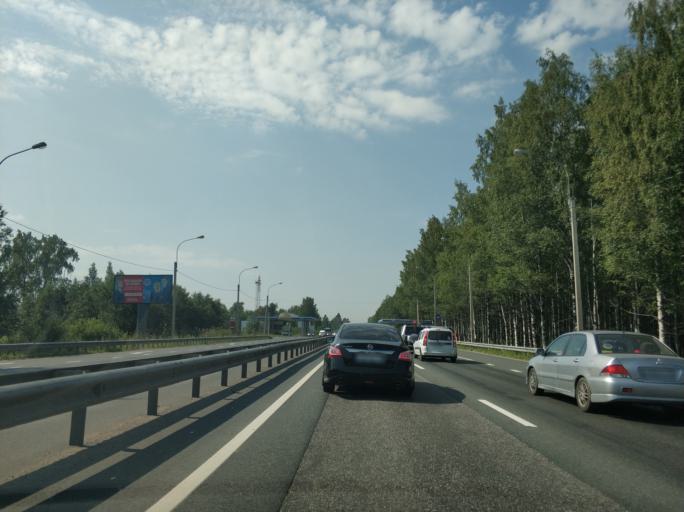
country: RU
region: St.-Petersburg
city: Krasnogvargeisky
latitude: 59.9951
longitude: 30.5409
